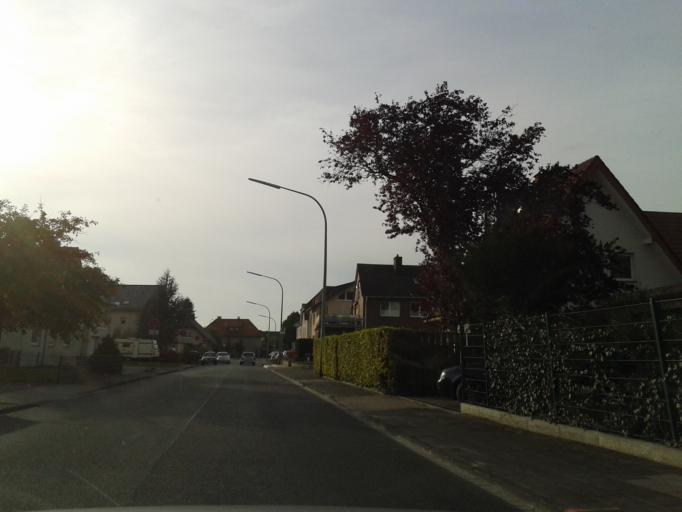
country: DE
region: North Rhine-Westphalia
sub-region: Regierungsbezirk Detmold
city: Paderborn
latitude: 51.7288
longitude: 8.6955
